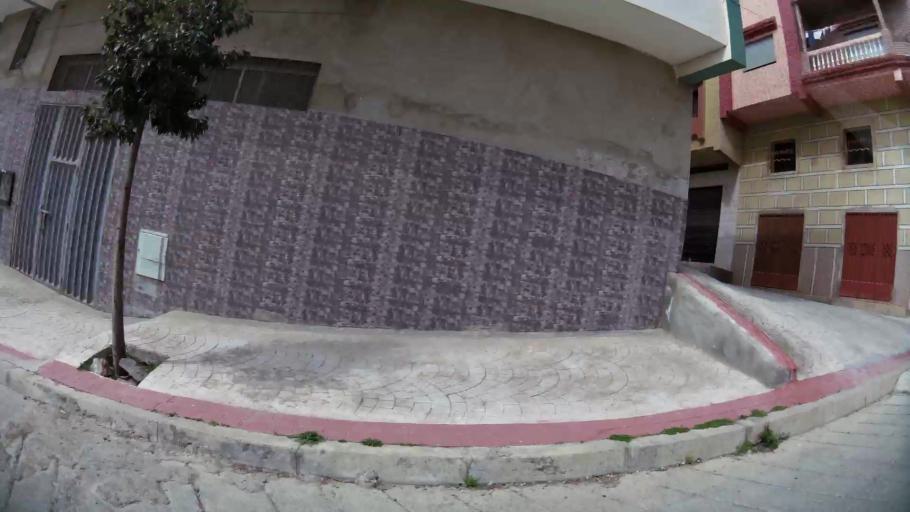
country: MA
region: Tanger-Tetouan
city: Tetouan
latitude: 35.5792
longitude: -5.3912
